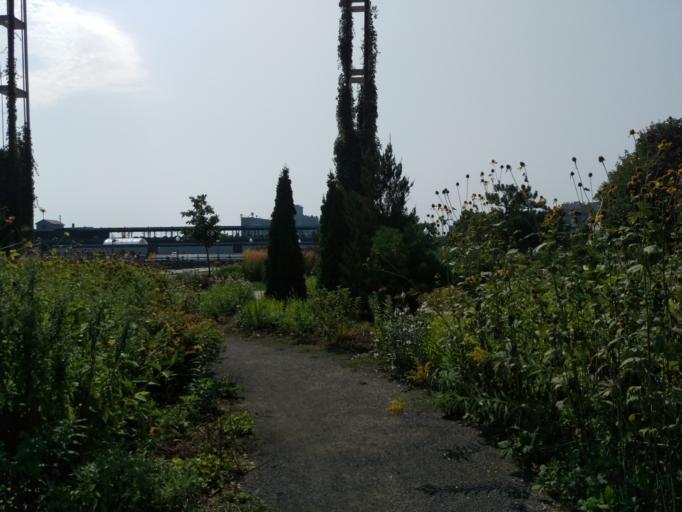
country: CA
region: Quebec
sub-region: Montreal
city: Montreal
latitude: 45.5049
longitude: -73.5530
